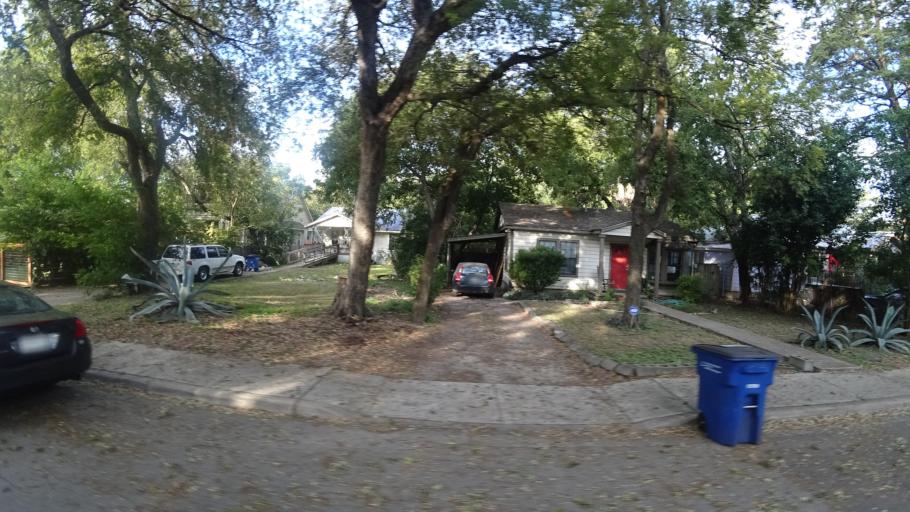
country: US
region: Texas
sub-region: Travis County
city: Austin
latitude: 30.2801
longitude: -97.7151
